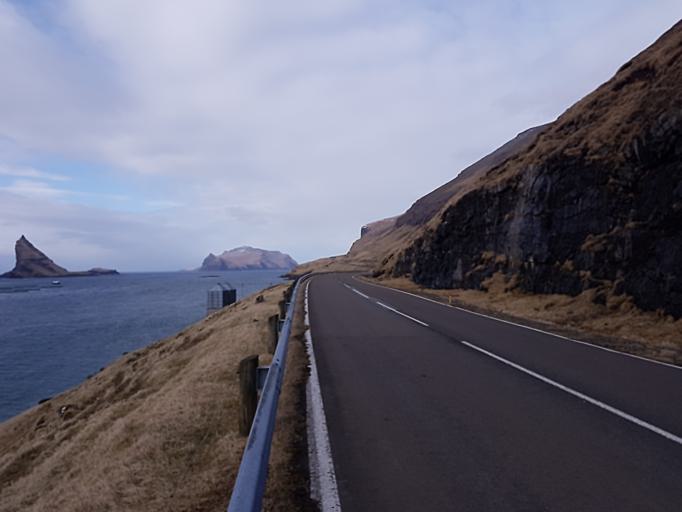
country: FO
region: Vagar
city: Sorvagur
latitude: 62.0820
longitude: -7.3578
